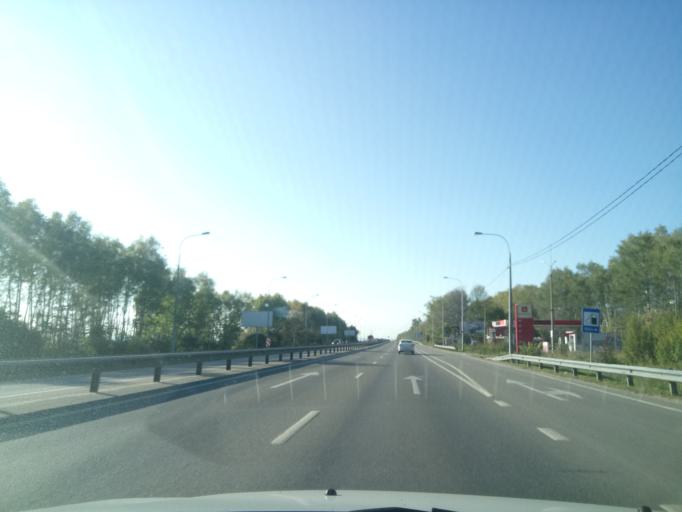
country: RU
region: Nizjnij Novgorod
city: Nizhniy Novgorod
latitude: 56.2094
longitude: 43.9278
